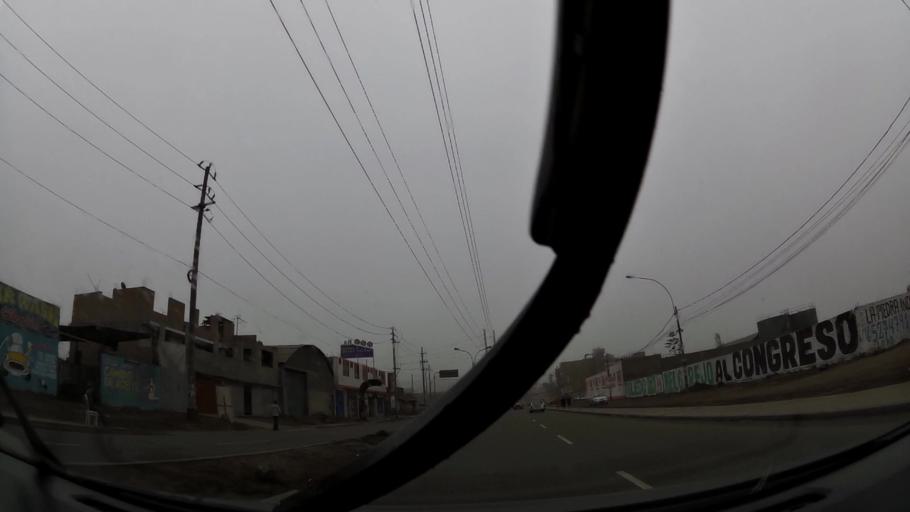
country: PE
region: Lima
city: Ventanilla
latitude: -11.8381
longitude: -77.1115
